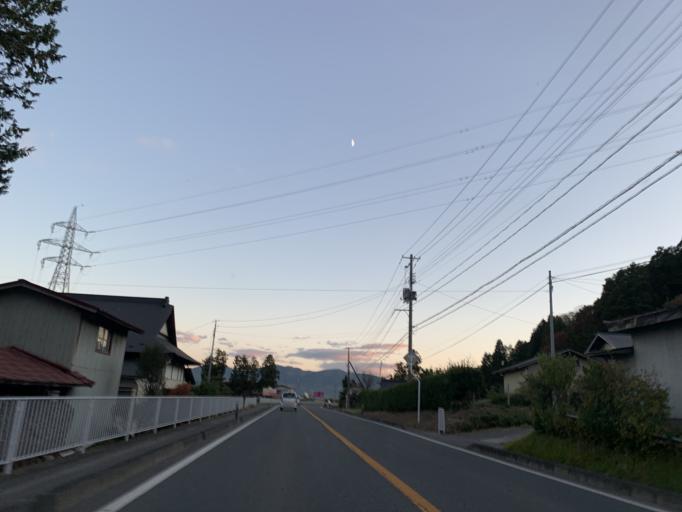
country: JP
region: Iwate
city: Mizusawa
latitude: 39.0898
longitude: 141.1360
